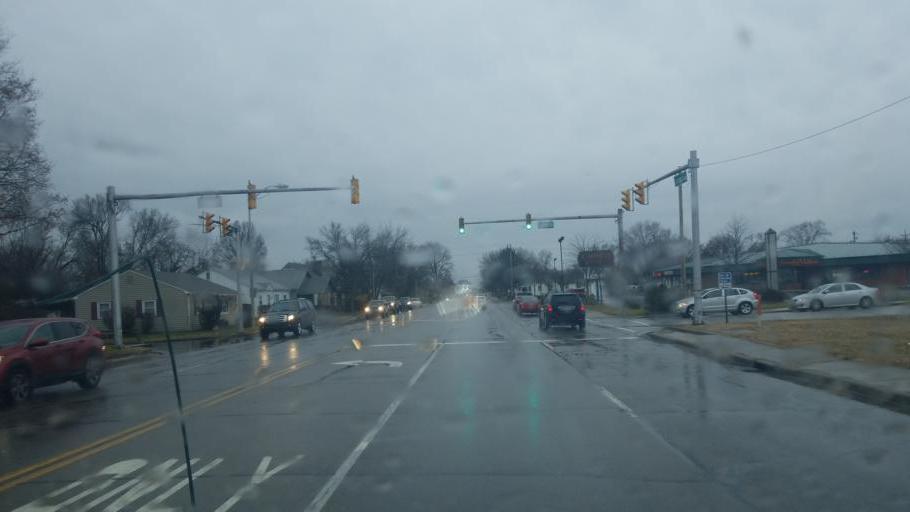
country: US
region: Indiana
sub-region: Bartholomew County
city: Columbus
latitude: 39.2206
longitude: -85.9042
